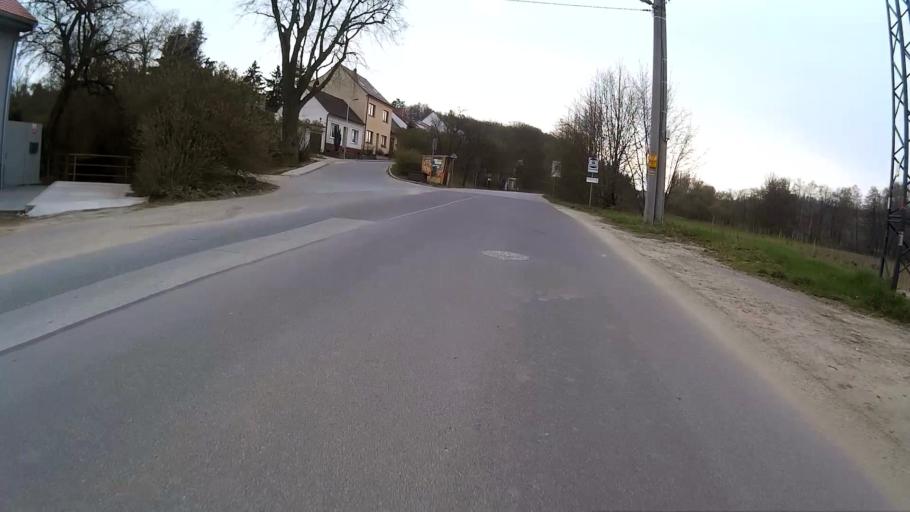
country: CZ
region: South Moravian
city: Ivancice
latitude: 49.0898
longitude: 16.3511
